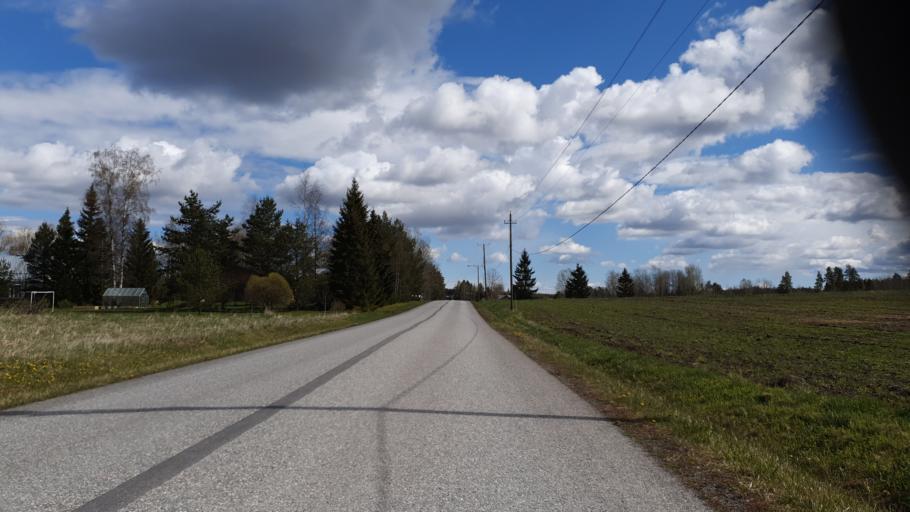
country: FI
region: Uusimaa
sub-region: Helsinki
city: Tuusula
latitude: 60.3895
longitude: 24.9066
